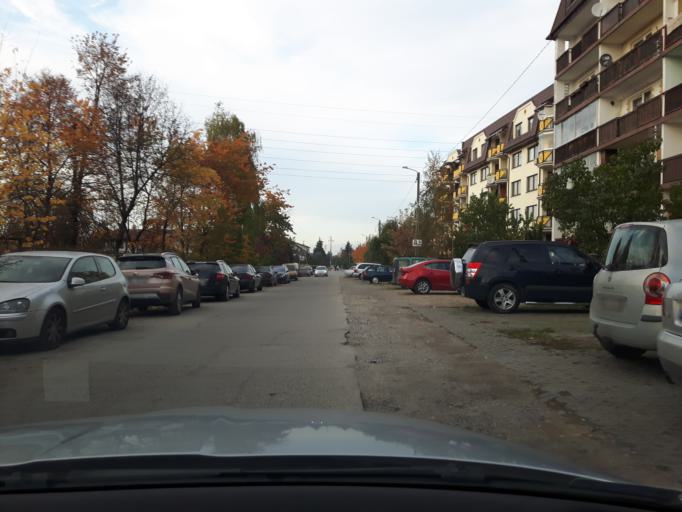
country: PL
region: Masovian Voivodeship
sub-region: Powiat wolominski
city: Zabki
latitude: 52.2795
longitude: 21.1190
